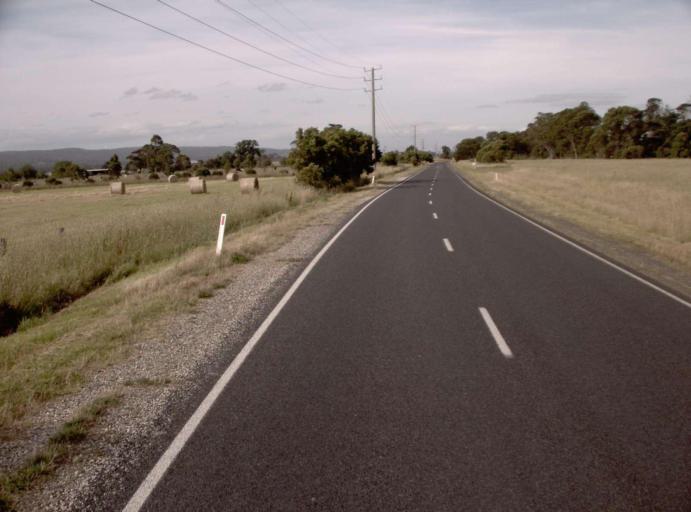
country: AU
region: Victoria
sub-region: Latrobe
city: Traralgon
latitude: -38.1016
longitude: 146.5938
